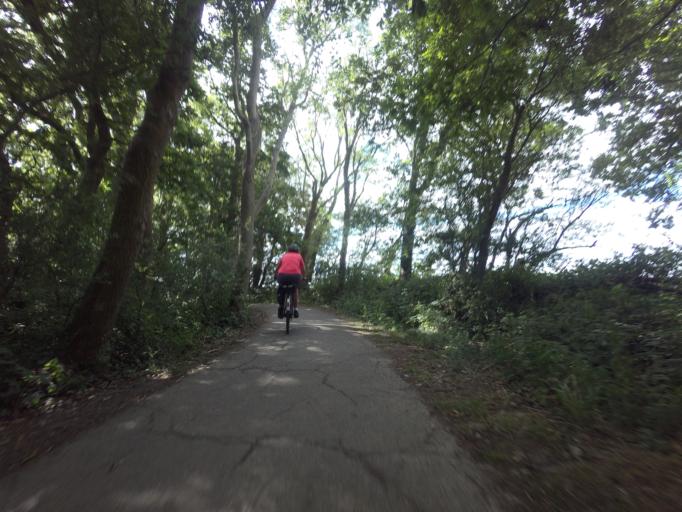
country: GB
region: England
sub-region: East Sussex
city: Hailsham
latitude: 50.8246
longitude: 0.2579
